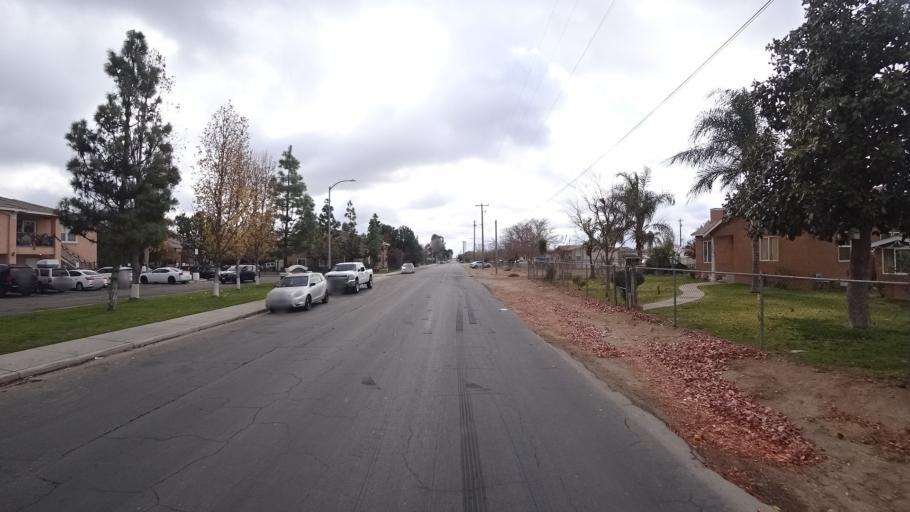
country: US
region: California
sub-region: Kern County
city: Bakersfield
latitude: 35.3377
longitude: -118.9899
